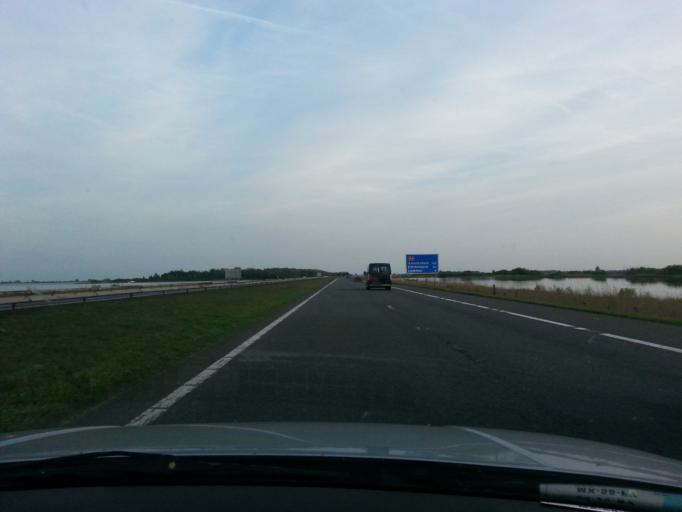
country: NL
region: Friesland
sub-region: Gemeente Skarsterlan
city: Sint Nicolaasga
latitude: 52.9109
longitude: 5.7733
